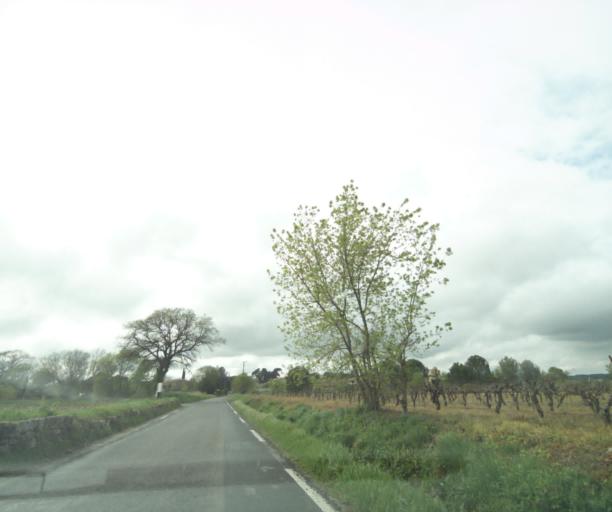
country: FR
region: Languedoc-Roussillon
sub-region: Departement de l'Herault
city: Saussan
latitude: 43.5695
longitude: 3.7810
